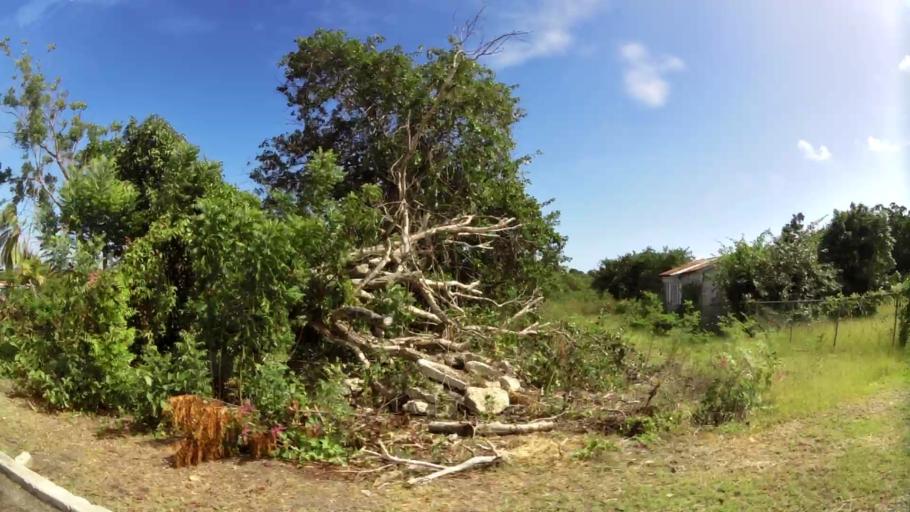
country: AG
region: Saint Paul
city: Falmouth
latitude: 17.0359
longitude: -61.7513
